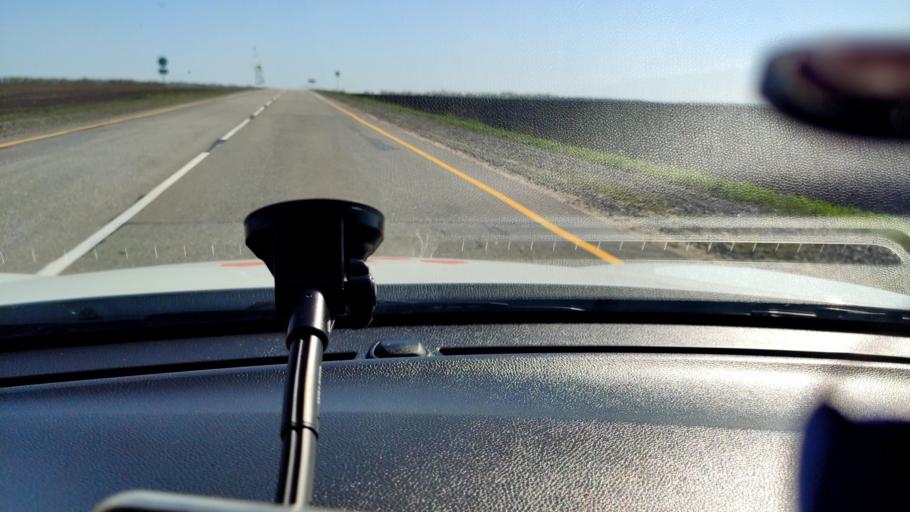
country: RU
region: Voronezj
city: Strelitsa
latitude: 51.4763
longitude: 38.9605
